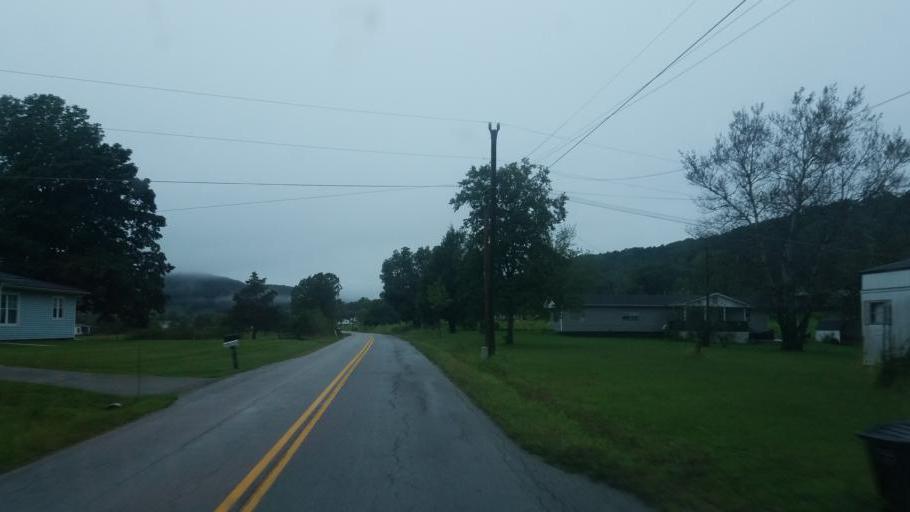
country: US
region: Kentucky
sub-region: Fleming County
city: Flemingsburg
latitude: 38.4036
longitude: -83.6307
